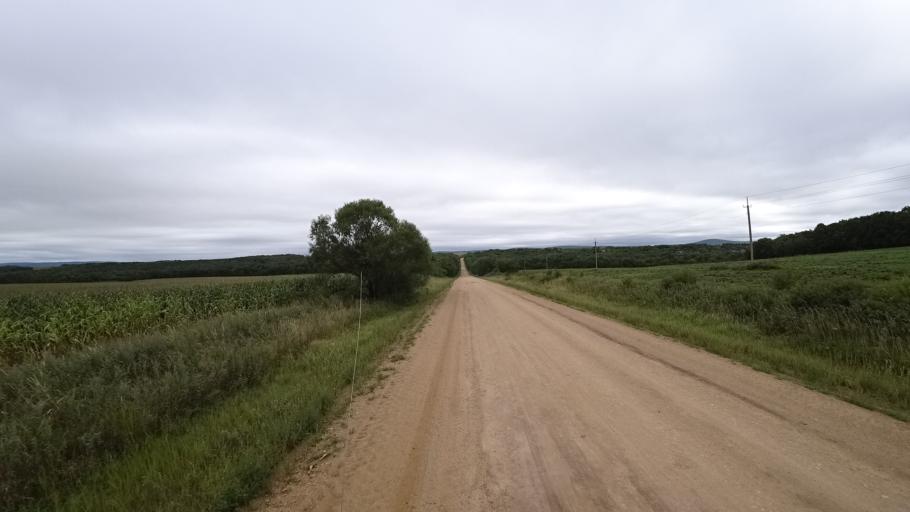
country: RU
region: Primorskiy
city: Monastyrishche
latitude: 44.0902
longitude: 132.5984
